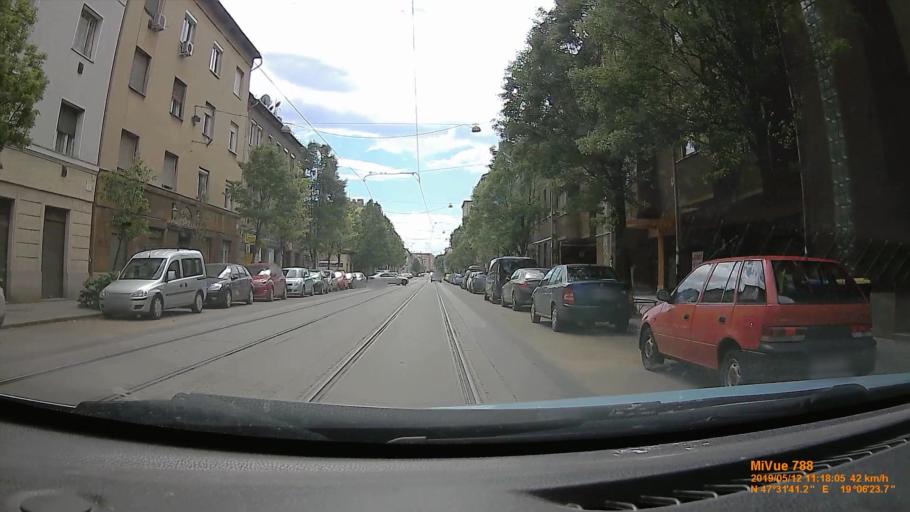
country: HU
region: Budapest
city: Budapest XIV. keruelet
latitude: 47.5280
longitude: 19.1065
